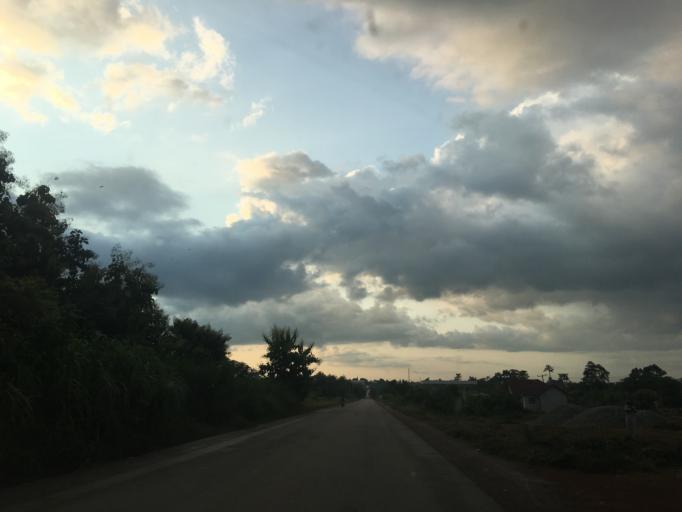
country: GH
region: Western
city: Bibiani
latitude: 6.7727
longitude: -2.5119
